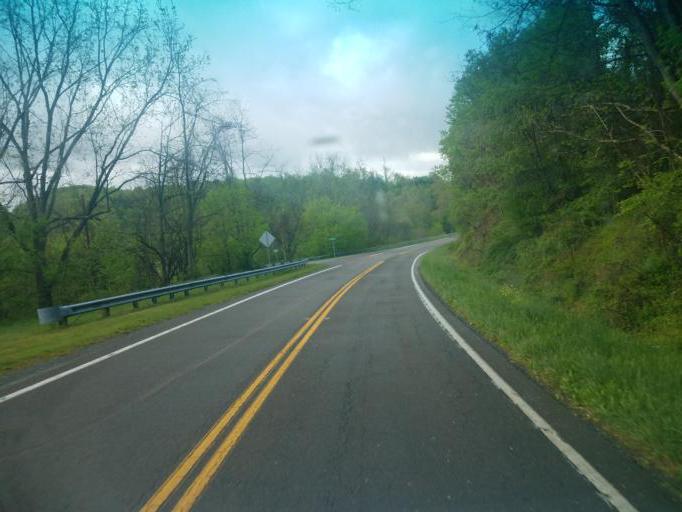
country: US
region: Virginia
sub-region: Washington County
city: Emory
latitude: 36.6690
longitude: -81.8029
